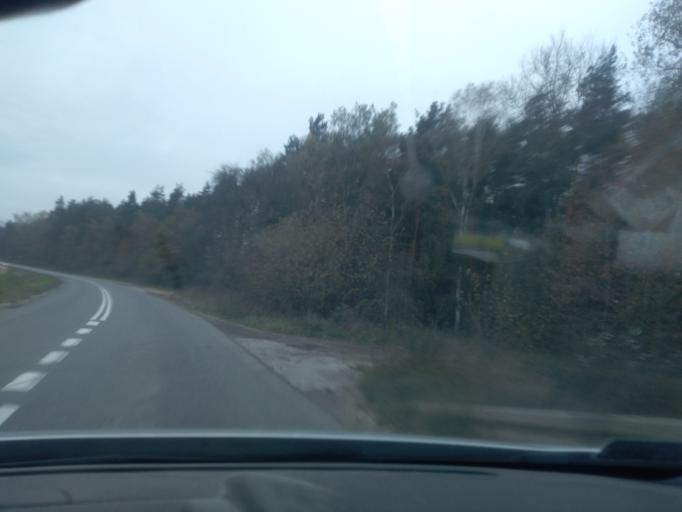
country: PL
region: Greater Poland Voivodeship
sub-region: Powiat poznanski
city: Murowana Goslina
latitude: 52.5567
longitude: 16.9753
